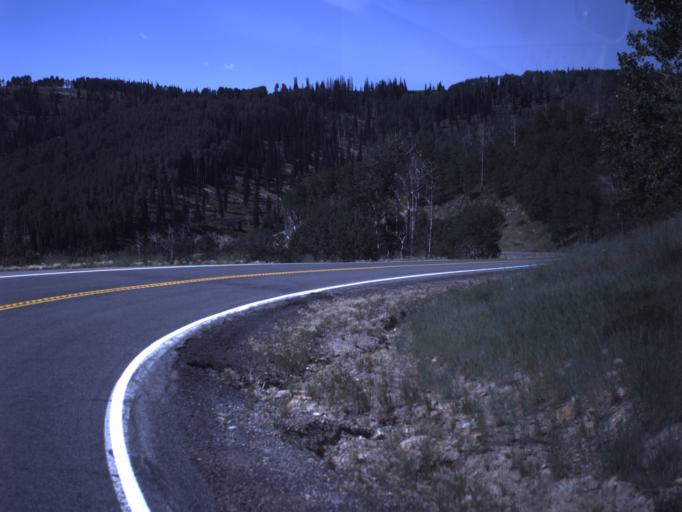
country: US
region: Utah
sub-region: Sanpete County
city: Fairview
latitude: 39.6830
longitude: -111.2111
